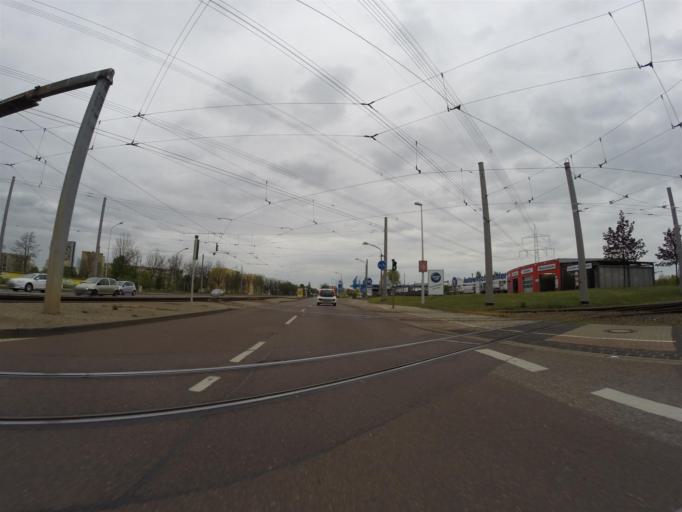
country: DE
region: Saxony-Anhalt
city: Schkopau
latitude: 51.4394
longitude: 11.9842
